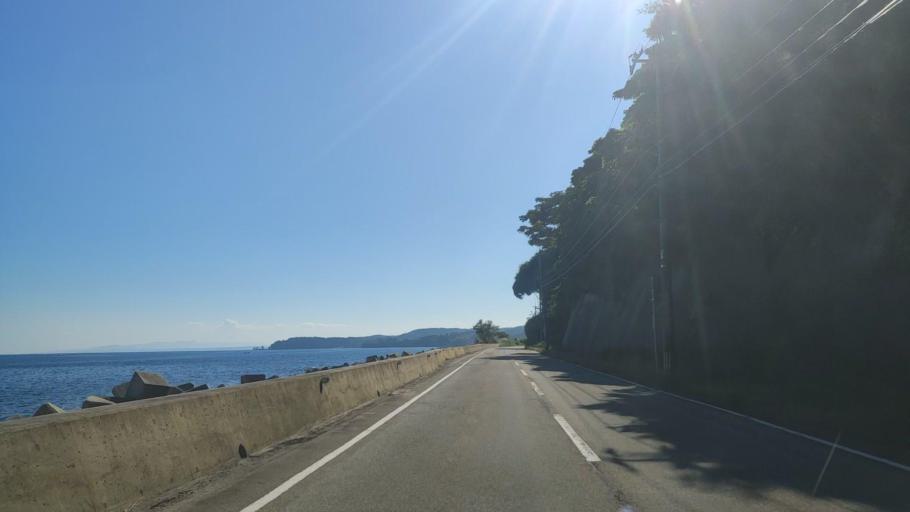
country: JP
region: Ishikawa
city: Nanao
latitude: 37.2819
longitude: 137.1084
